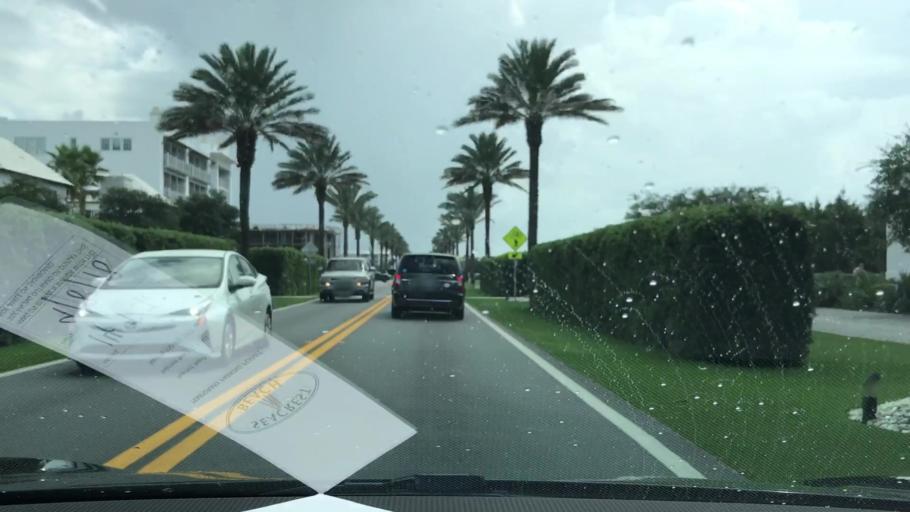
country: US
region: Florida
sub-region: Bay County
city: Laguna Beach
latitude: 30.2851
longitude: -86.0300
